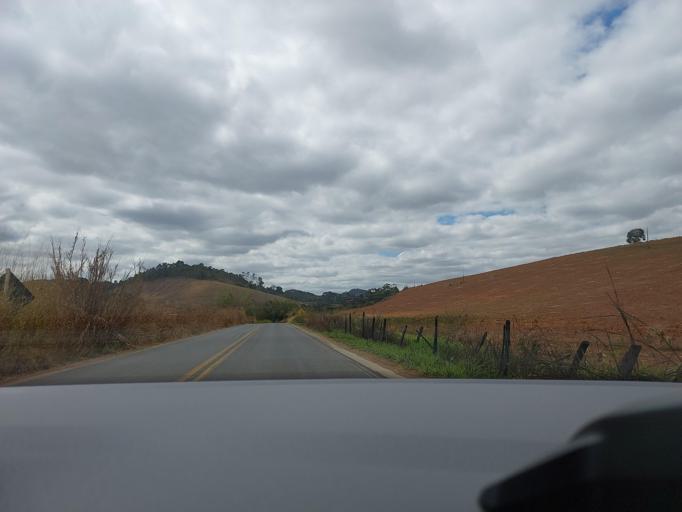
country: BR
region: Minas Gerais
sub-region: Vicosa
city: Vicosa
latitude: -20.8290
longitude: -42.7479
